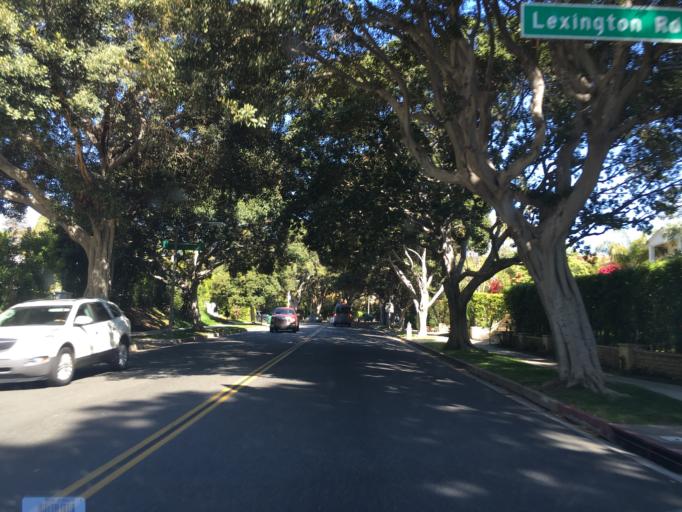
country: US
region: California
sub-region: Los Angeles County
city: Beverly Hills
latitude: 34.0857
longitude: -118.4128
